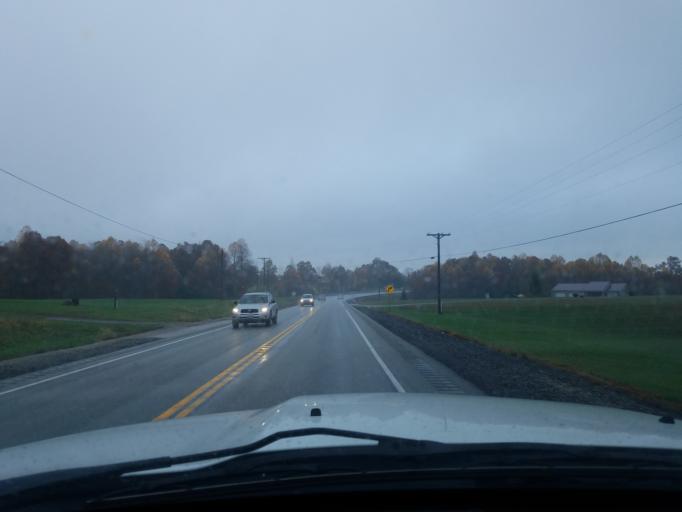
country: US
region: Kentucky
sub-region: Larue County
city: Hodgenville
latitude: 37.4692
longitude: -85.5878
